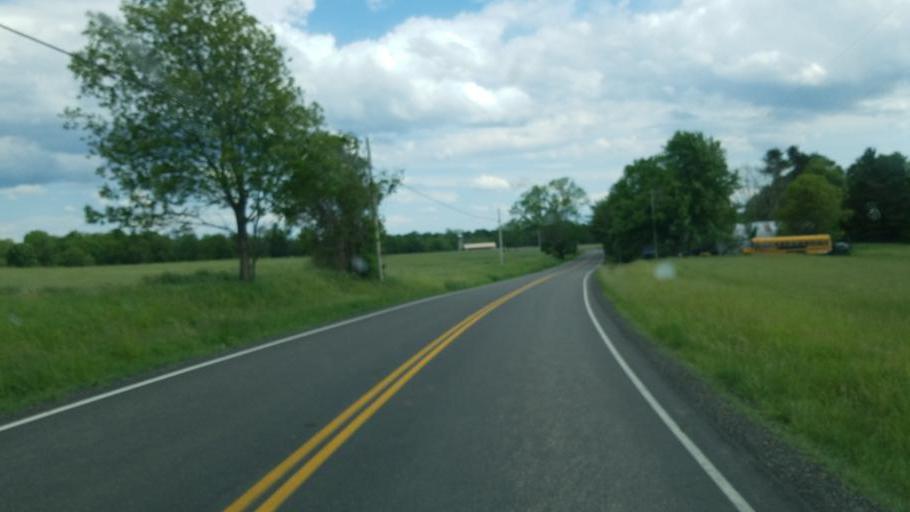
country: US
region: Ohio
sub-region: Huron County
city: Greenwich
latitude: 40.9340
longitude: -82.5404
